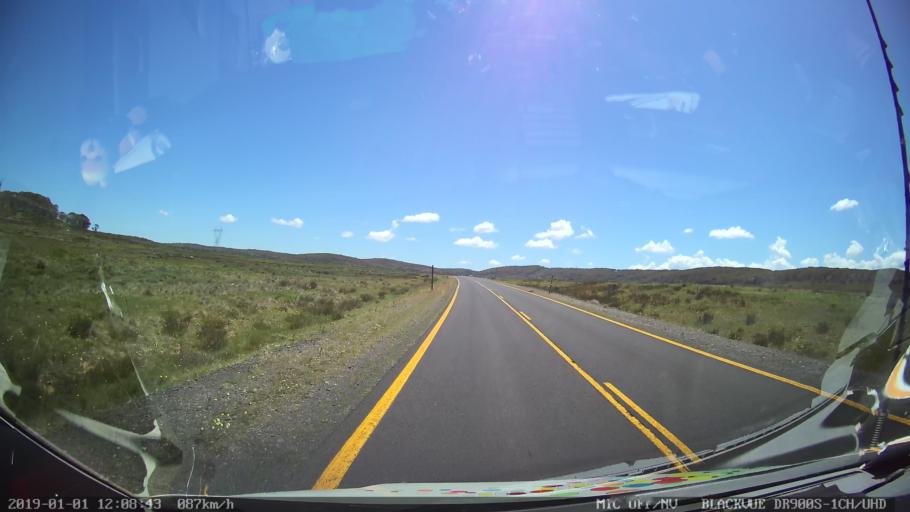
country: AU
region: New South Wales
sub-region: Tumut Shire
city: Tumut
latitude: -35.8168
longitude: 148.4960
